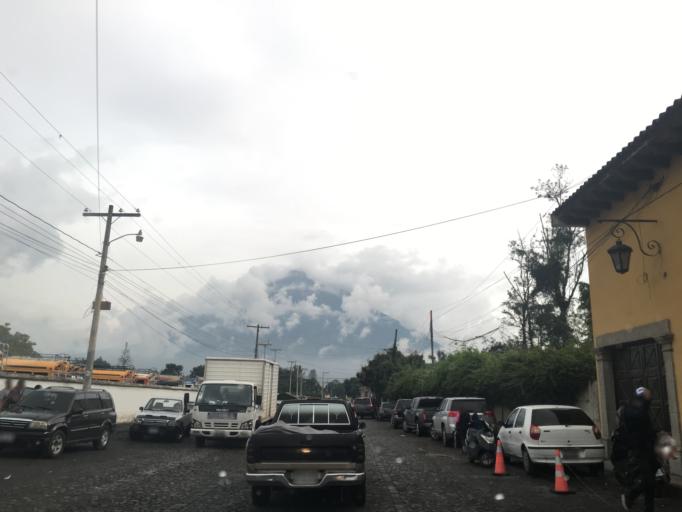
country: GT
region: Sacatepequez
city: Antigua Guatemala
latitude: 14.5589
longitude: -90.7408
